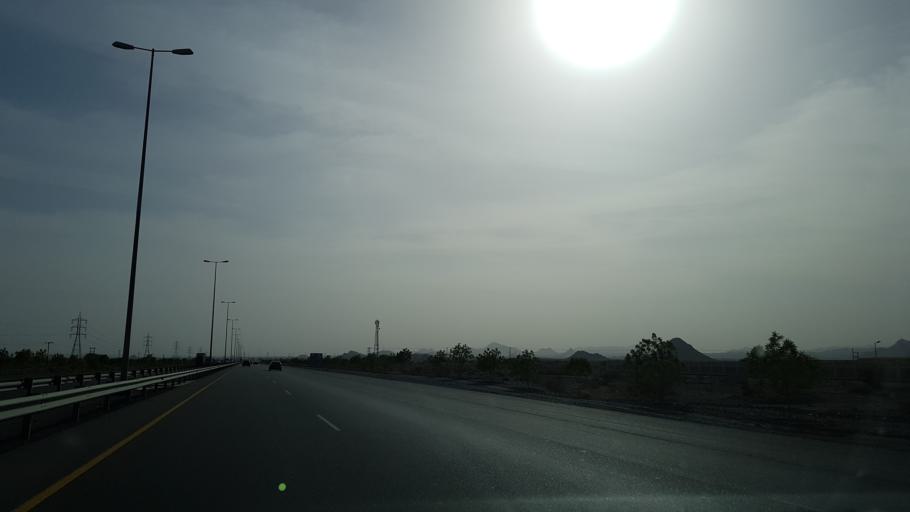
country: OM
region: Muhafazat ad Dakhiliyah
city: Nizwa
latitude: 22.8665
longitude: 57.6009
